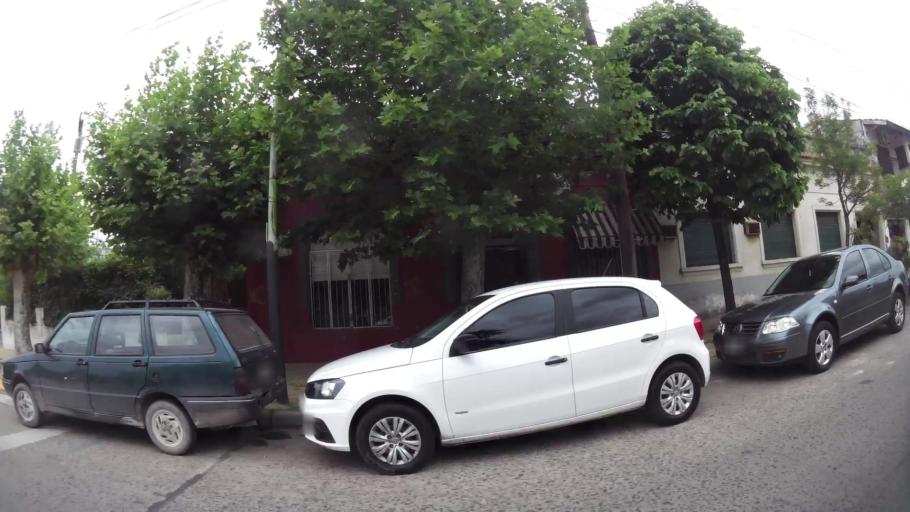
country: AR
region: Buenos Aires
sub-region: Partido de Campana
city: Campana
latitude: -34.1635
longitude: -58.9583
